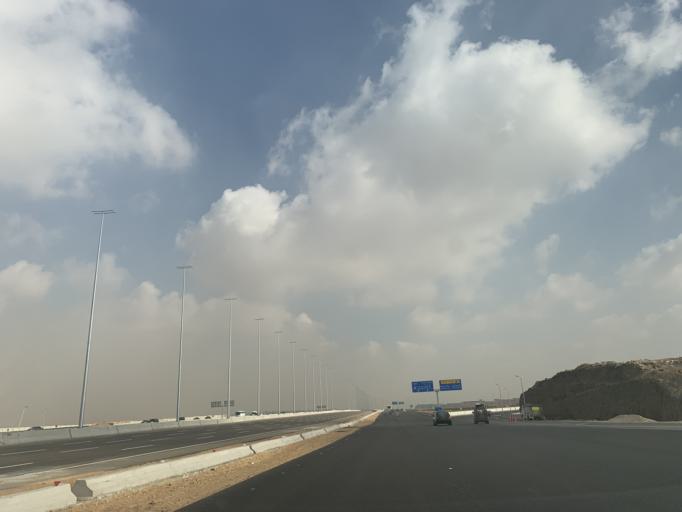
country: EG
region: Muhafazat al Qalyubiyah
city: Al Khankah
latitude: 30.0825
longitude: 31.4504
